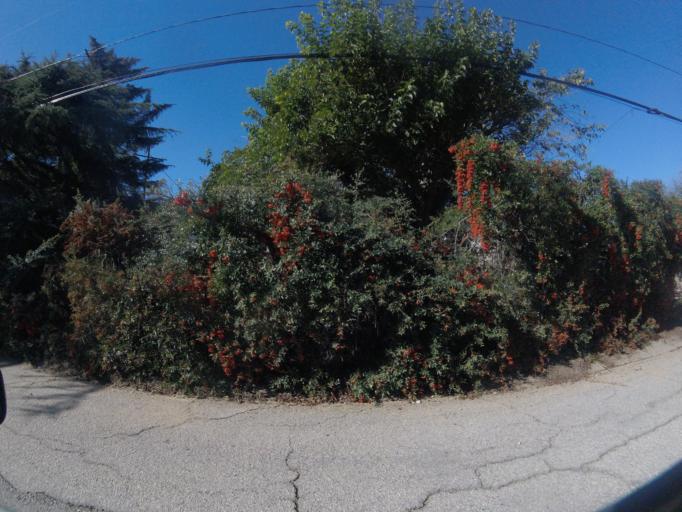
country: US
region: California
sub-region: San Bernardino County
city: Mentone
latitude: 34.0222
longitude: -117.1118
